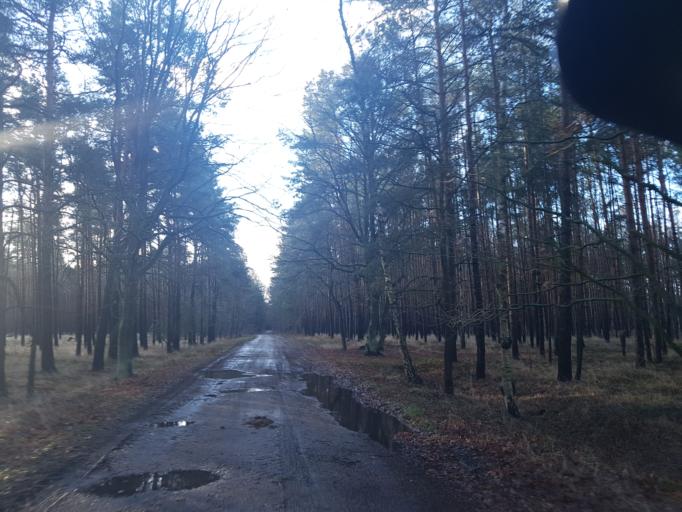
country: DE
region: Brandenburg
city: Ruckersdorf
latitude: 51.5916
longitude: 13.6028
